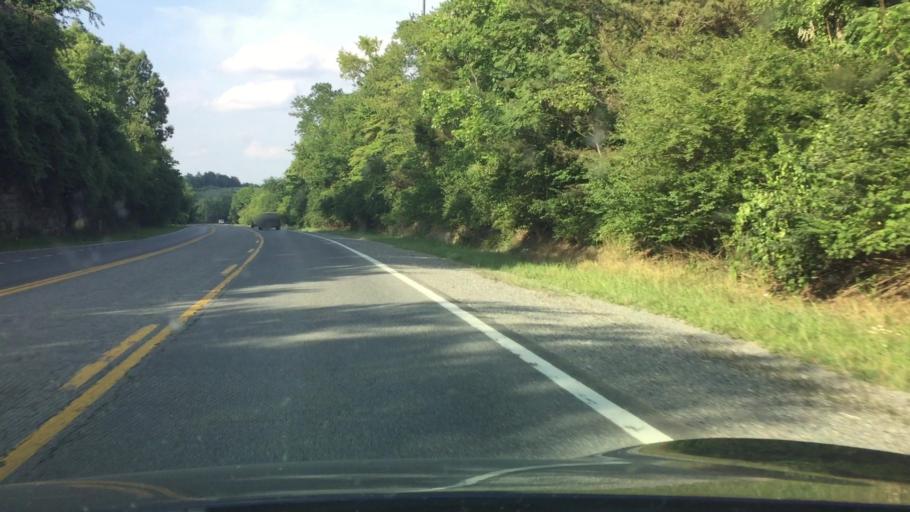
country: US
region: Virginia
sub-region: Pulaski County
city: Dublin
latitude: 37.1233
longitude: -80.6525
